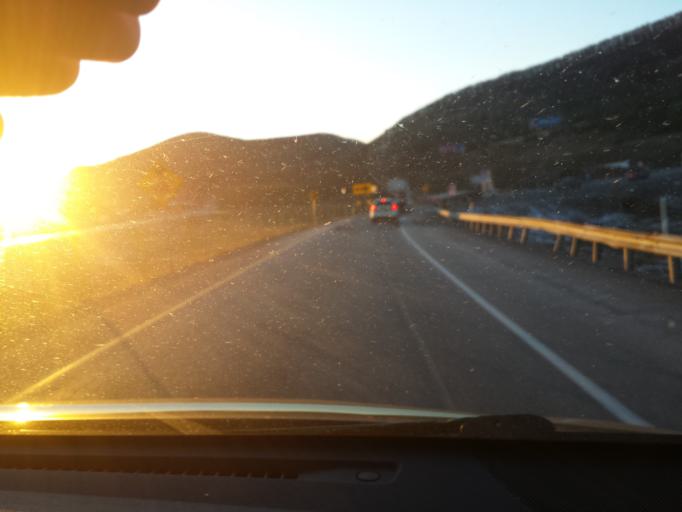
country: US
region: Pennsylvania
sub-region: Centre County
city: Zion
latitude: 40.9459
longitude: -77.7151
